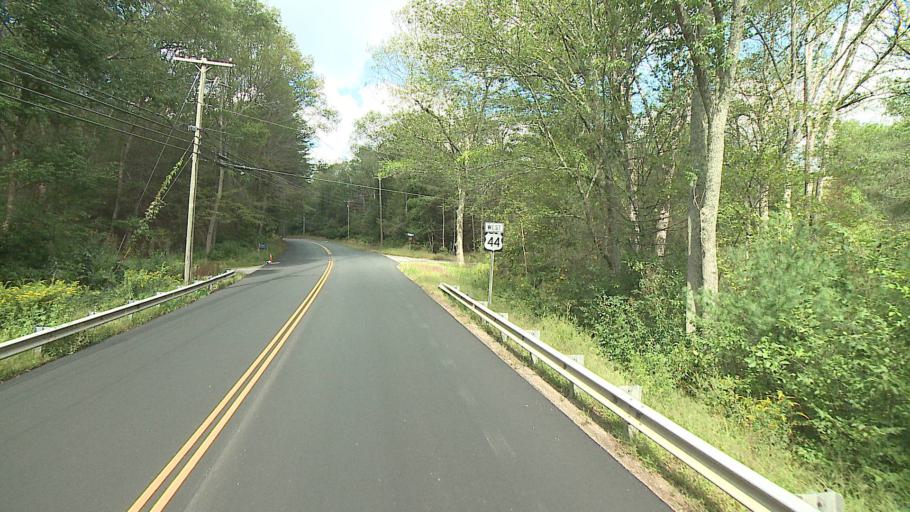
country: US
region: Connecticut
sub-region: Windham County
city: Thompson
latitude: 41.9221
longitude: -71.8418
